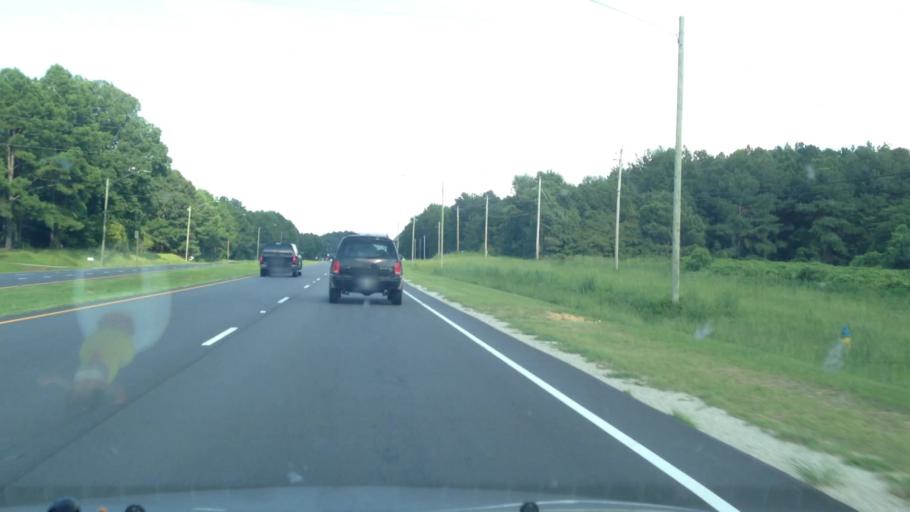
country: US
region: North Carolina
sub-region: Harnett County
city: Lillington
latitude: 35.4105
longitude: -78.7846
